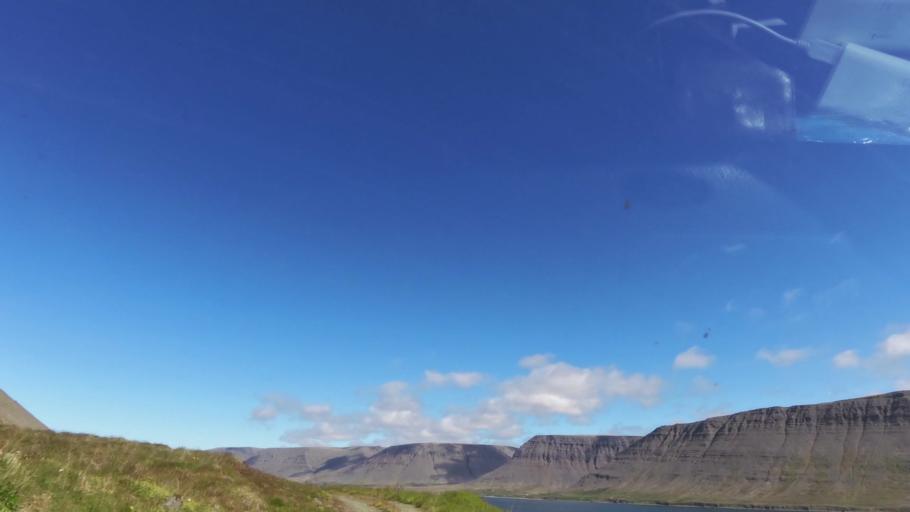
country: IS
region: West
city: Olafsvik
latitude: 65.6249
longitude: -23.8959
